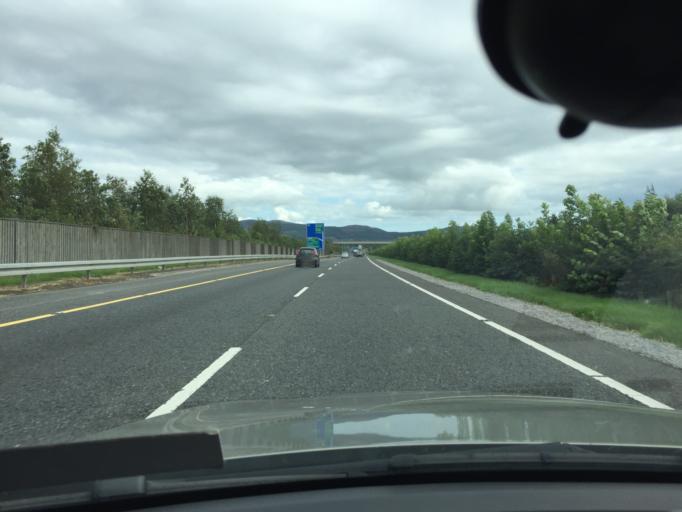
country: IE
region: Leinster
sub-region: Lu
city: Dundalk
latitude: 54.0366
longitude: -6.4057
